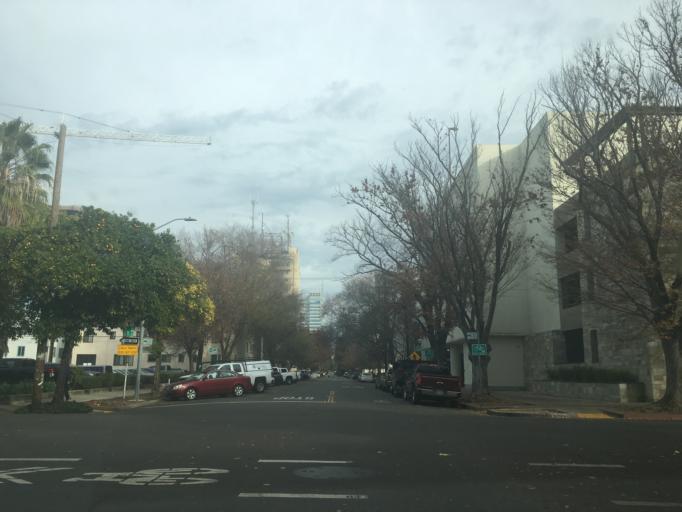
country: US
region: California
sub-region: Sacramento County
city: Sacramento
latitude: 38.5724
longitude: -121.4922
